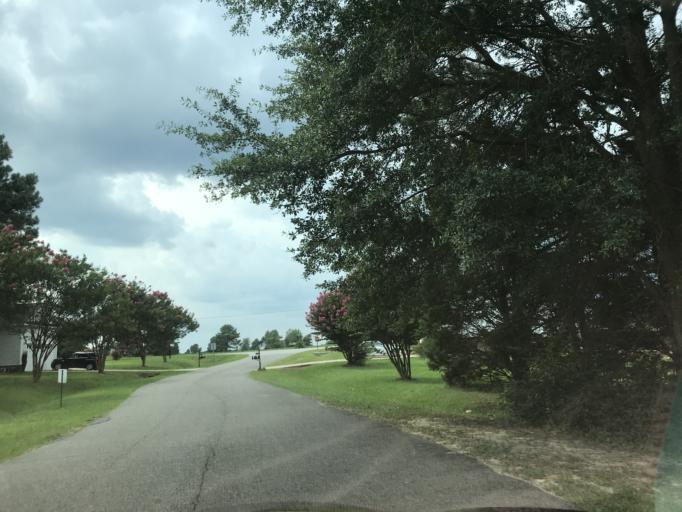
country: US
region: North Carolina
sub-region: Johnston County
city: Four Oaks
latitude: 35.5132
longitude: -78.5032
